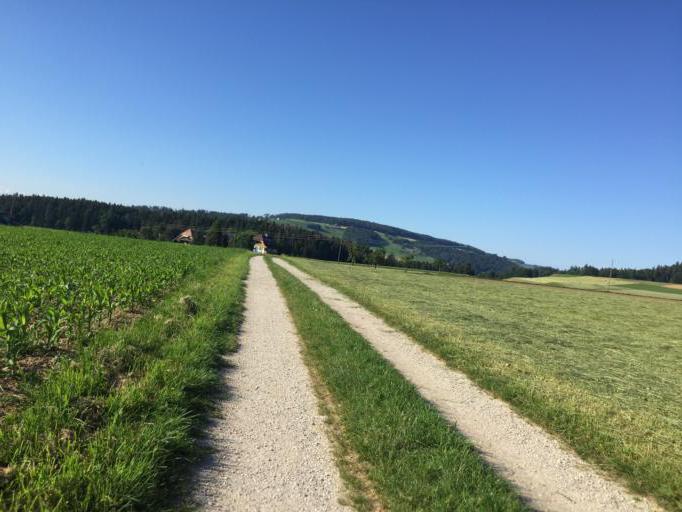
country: CH
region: Bern
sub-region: Bern-Mittelland District
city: Niederwichtrach
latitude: 46.8596
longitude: 7.5916
